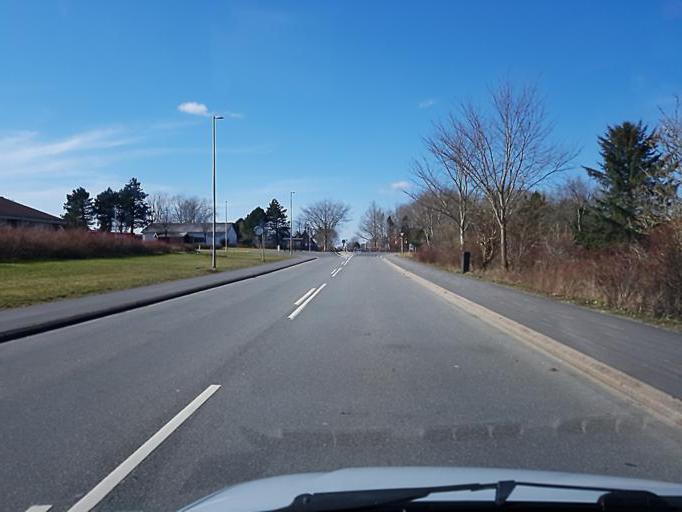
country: DK
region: South Denmark
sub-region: Varde Kommune
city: Varde
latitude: 55.6099
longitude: 8.4997
